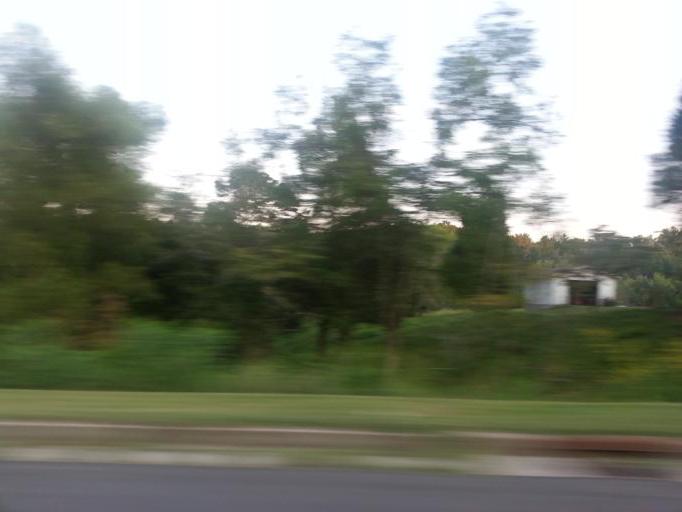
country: US
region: Tennessee
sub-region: Roane County
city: Kingston
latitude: 35.8949
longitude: -84.4108
